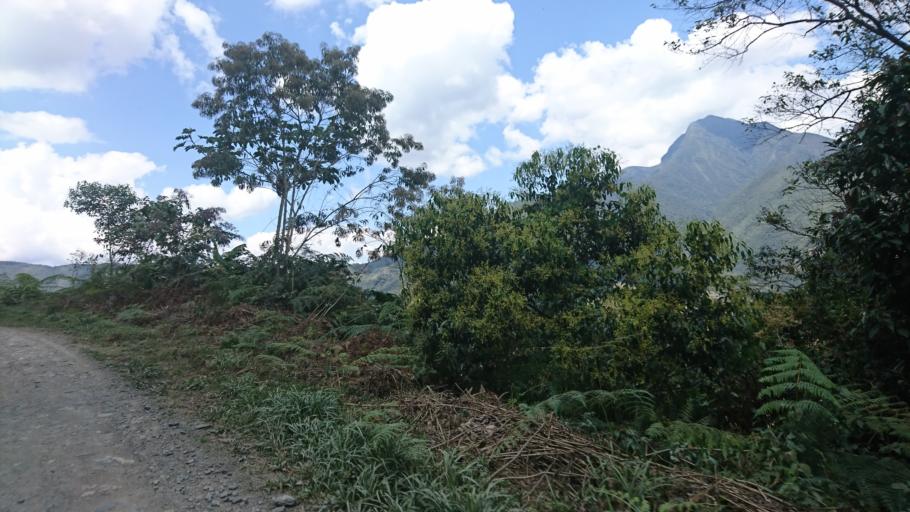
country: BO
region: La Paz
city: Coroico
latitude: -16.0980
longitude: -67.7835
